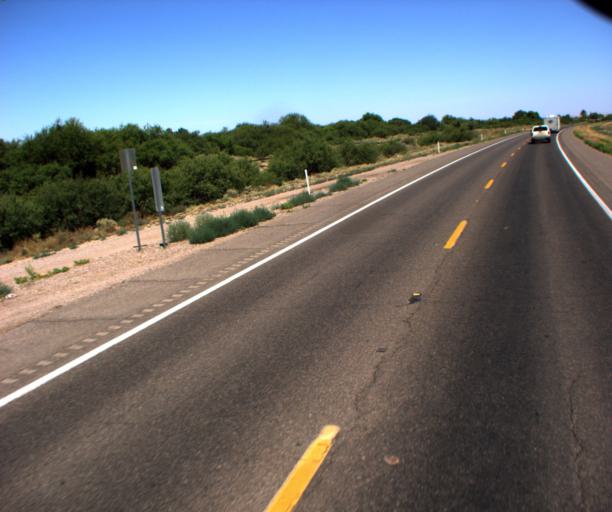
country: US
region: Arizona
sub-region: Graham County
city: Pima
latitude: 32.9407
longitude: -109.9067
